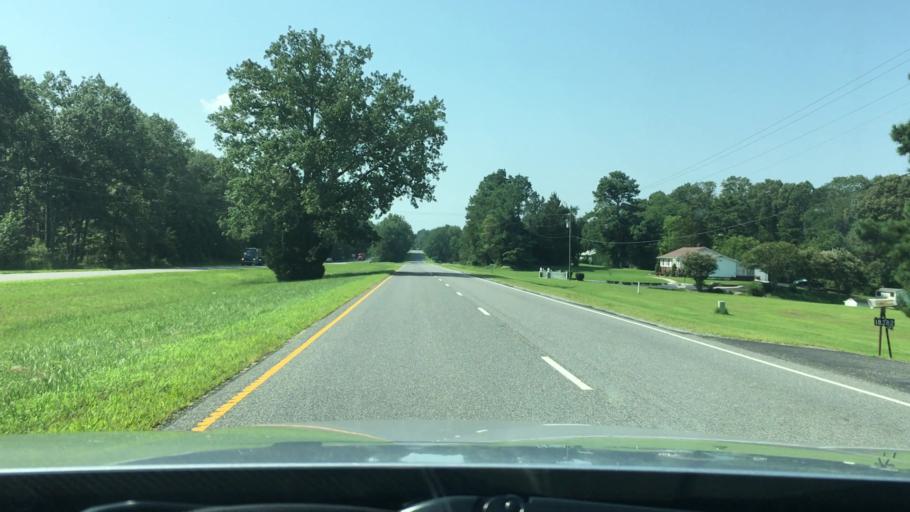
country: US
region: Virginia
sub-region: Caroline County
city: Bowling Green
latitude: 38.0095
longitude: -77.4135
